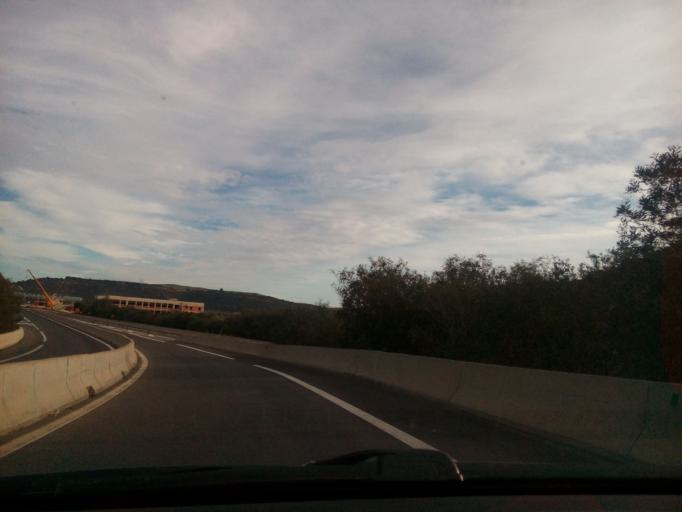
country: DZ
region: Sidi Bel Abbes
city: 'Ain el Berd
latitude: 35.3811
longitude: -0.4995
